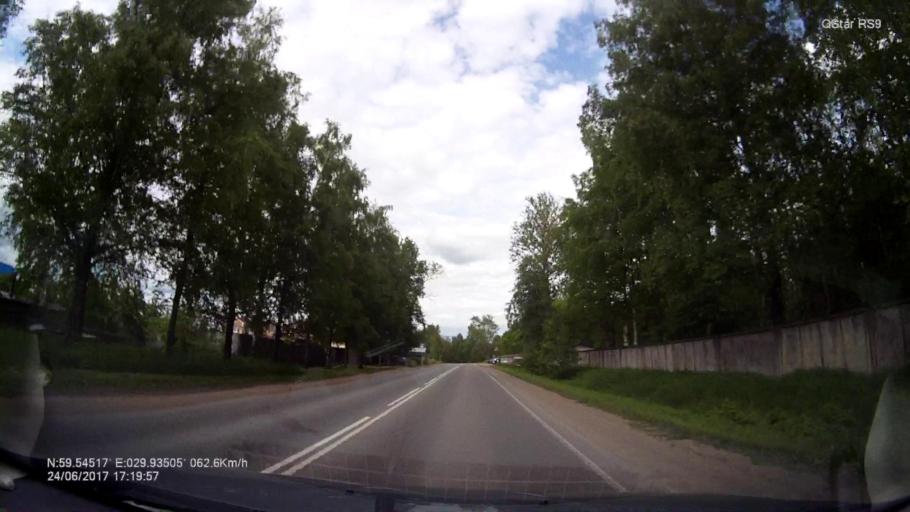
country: RU
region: Leningrad
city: Voyskovitsy
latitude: 59.5453
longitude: 29.9357
